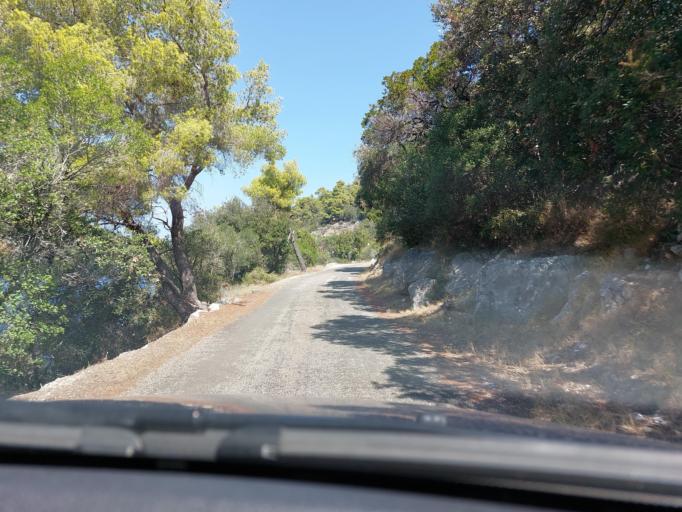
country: HR
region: Dubrovacko-Neretvanska
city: Smokvica
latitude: 42.7711
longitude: 16.8375
